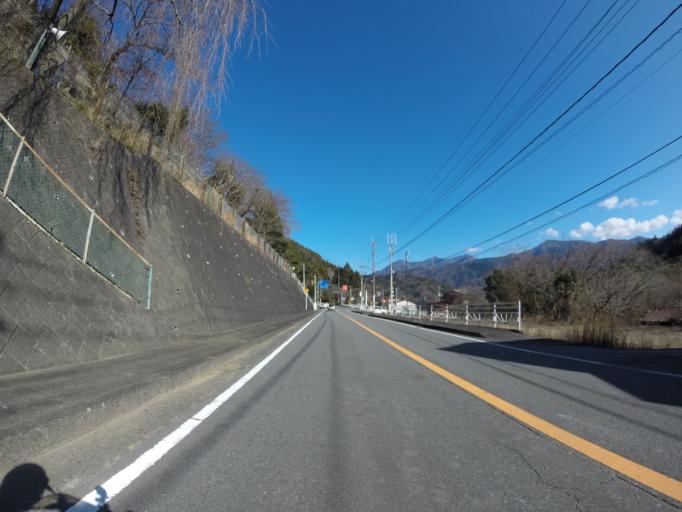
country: JP
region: Shizuoka
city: Fujinomiya
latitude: 35.3671
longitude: 138.4252
